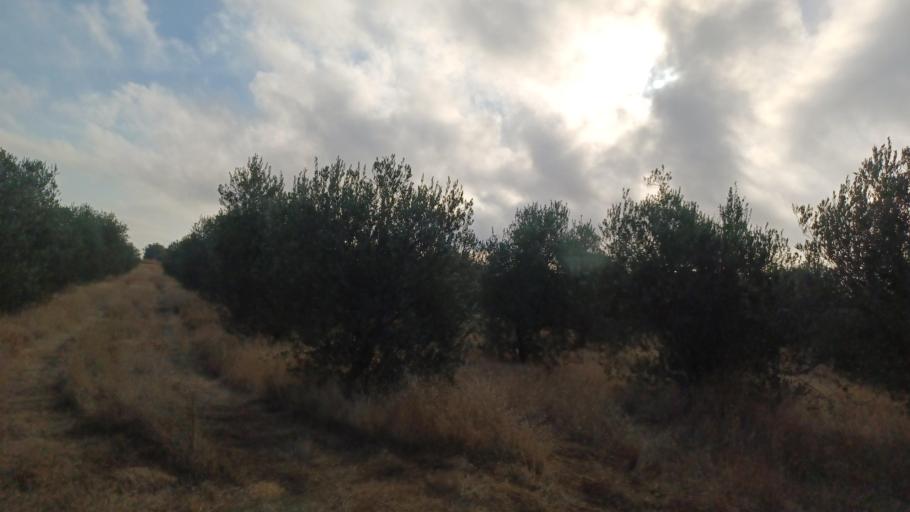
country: CY
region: Ammochostos
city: Avgorou
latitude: 35.0437
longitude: 33.8518
